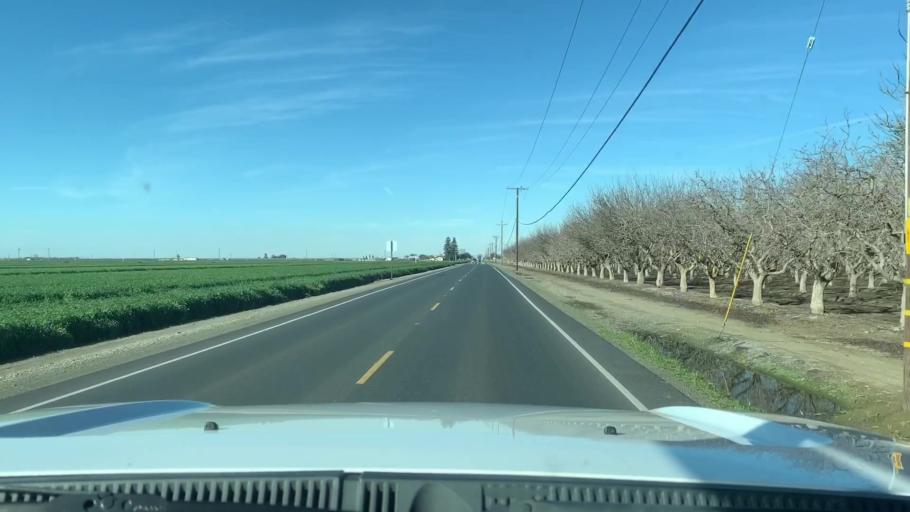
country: US
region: California
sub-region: Kings County
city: Corcoran
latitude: 36.1820
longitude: -119.4933
